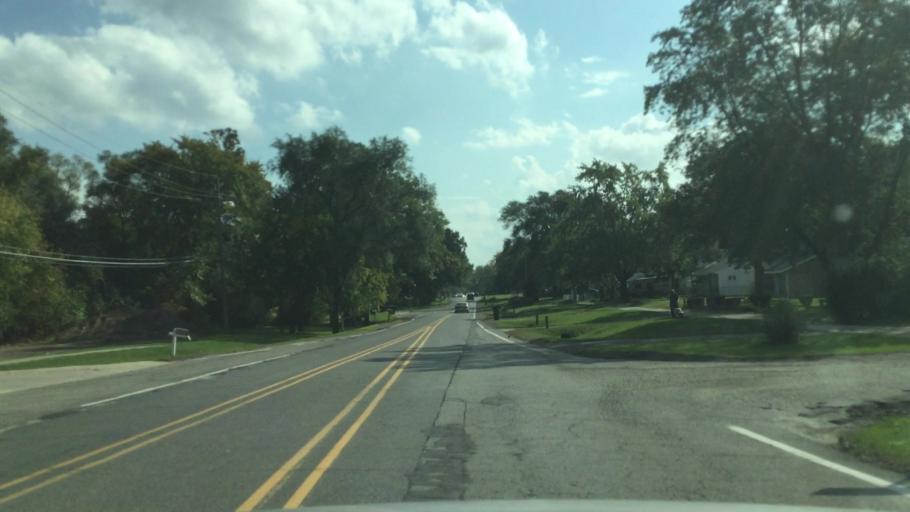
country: US
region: Michigan
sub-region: Oakland County
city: Waterford
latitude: 42.6568
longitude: -83.3861
